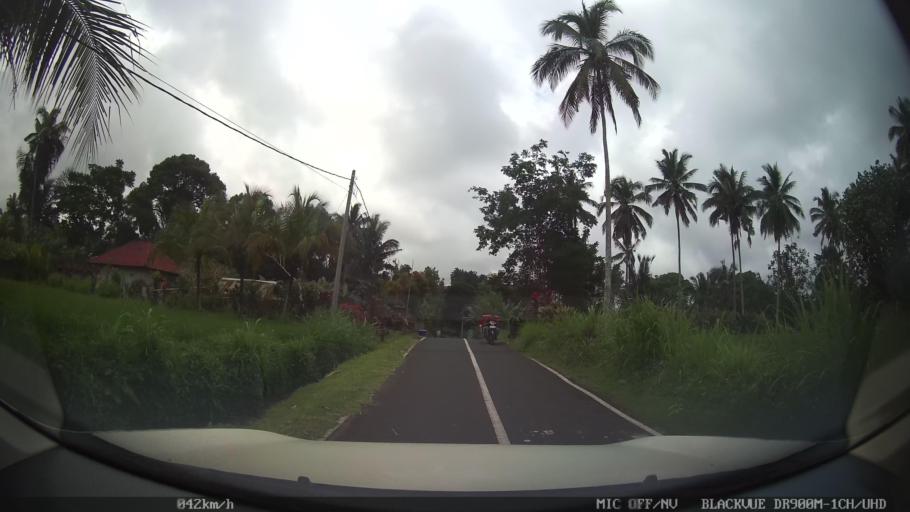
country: ID
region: Bali
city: Pemijian
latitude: -8.4529
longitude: 115.2299
